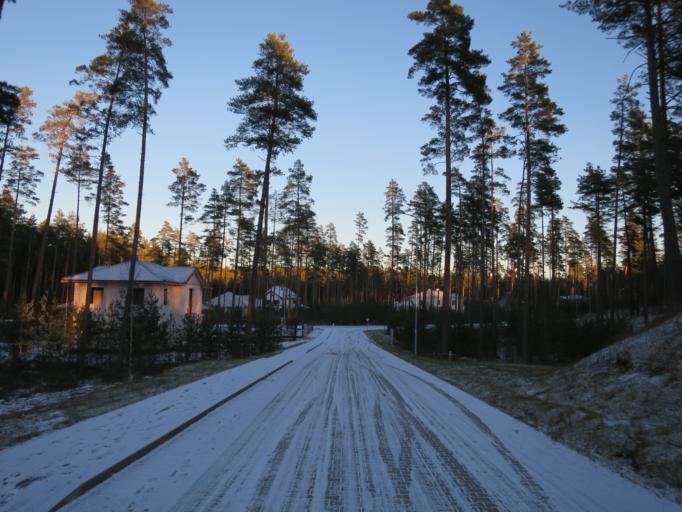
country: LV
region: Riga
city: Bergi
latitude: 56.9809
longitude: 24.3142
